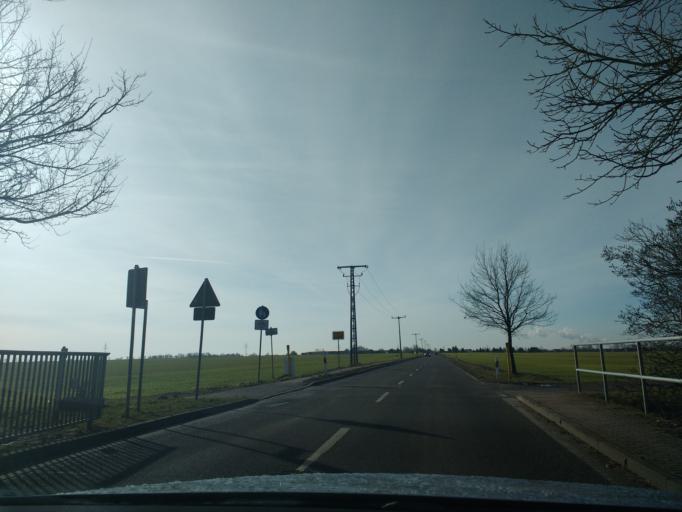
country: DE
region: Saxony-Anhalt
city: Braschwitz
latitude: 51.5335
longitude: 12.0607
